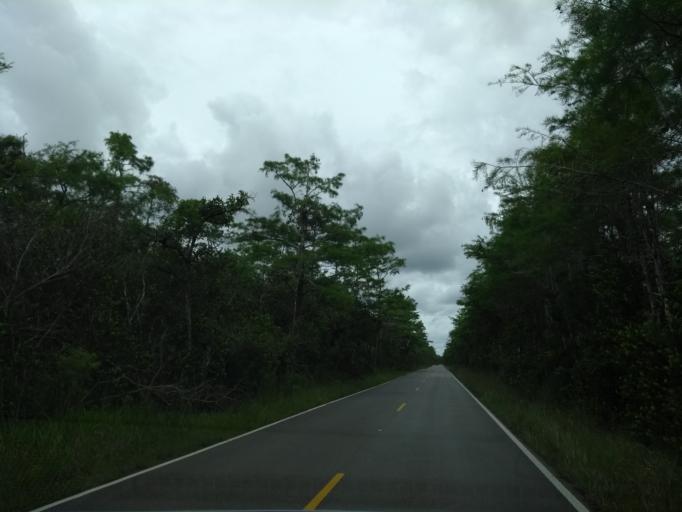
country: US
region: Florida
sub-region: Miami-Dade County
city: The Hammocks
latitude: 25.7613
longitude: -80.9116
